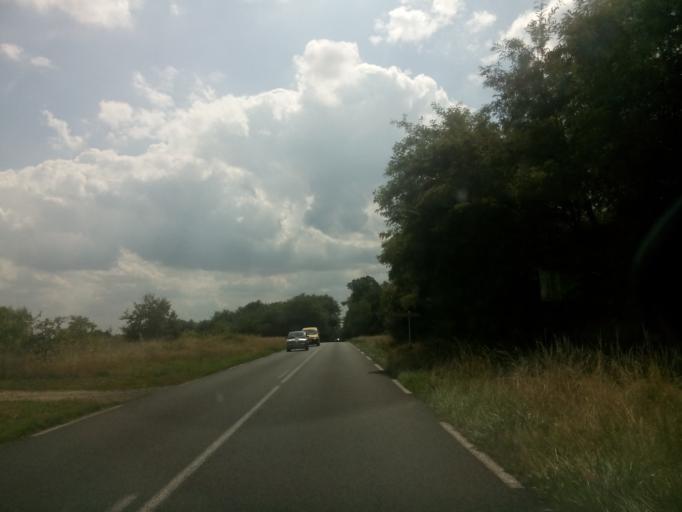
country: FR
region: Centre
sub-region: Departement d'Indre-et-Loire
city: Cheille
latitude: 47.2827
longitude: 0.4241
